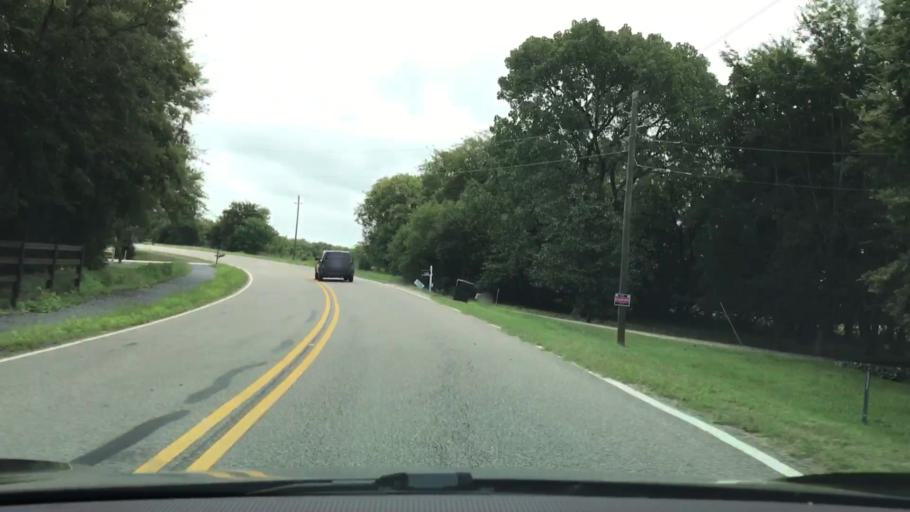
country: US
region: Alabama
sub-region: Montgomery County
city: Pike Road
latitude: 32.3027
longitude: -86.0520
